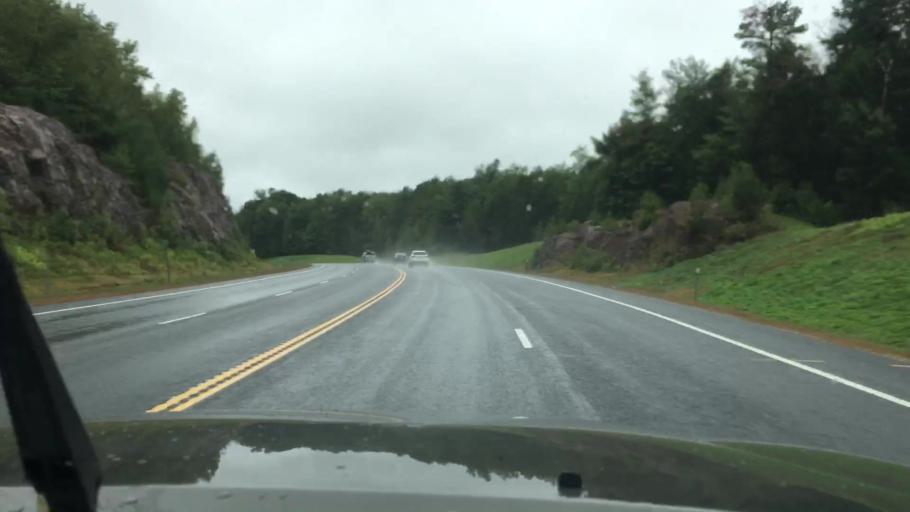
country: US
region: New Hampshire
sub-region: Cheshire County
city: Harrisville
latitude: 43.0074
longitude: -72.1650
